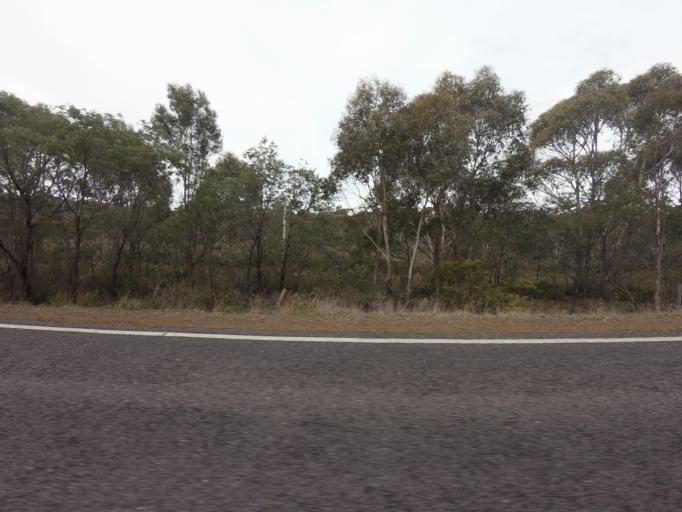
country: AU
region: Tasmania
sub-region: Sorell
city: Sorell
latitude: -42.4106
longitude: 147.9337
